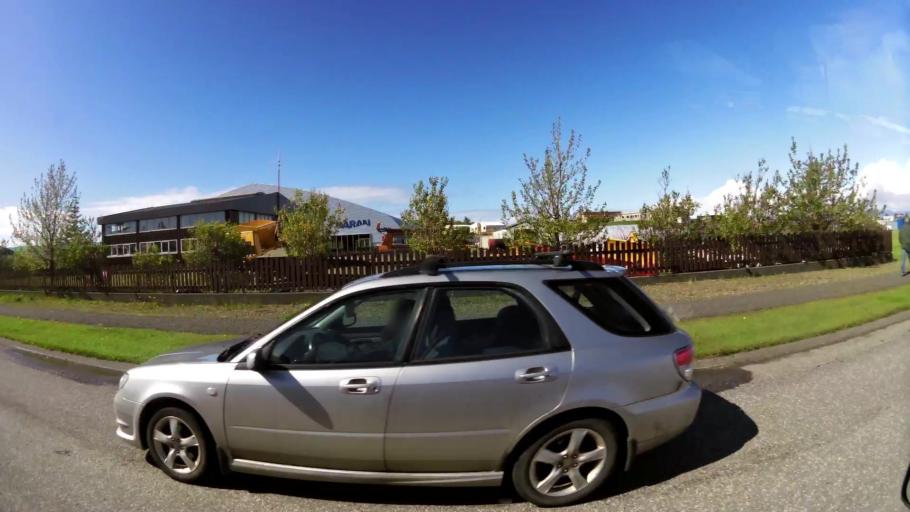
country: IS
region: East
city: Hoefn
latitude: 64.2527
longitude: -15.2039
